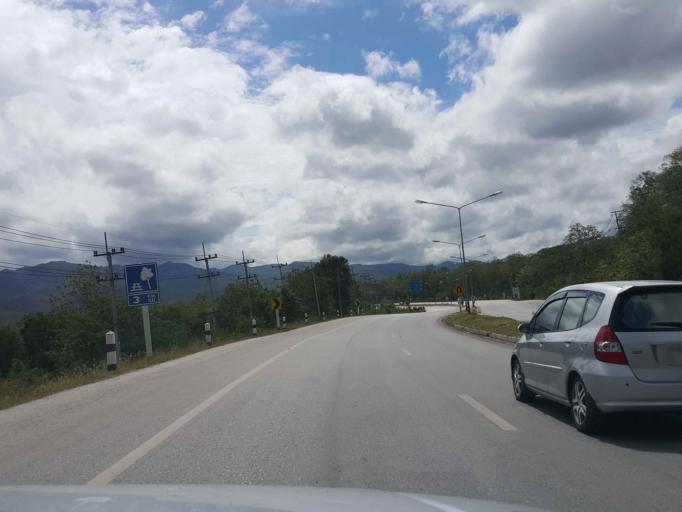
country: TH
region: Tak
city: Tak
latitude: 16.8047
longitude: 99.0499
